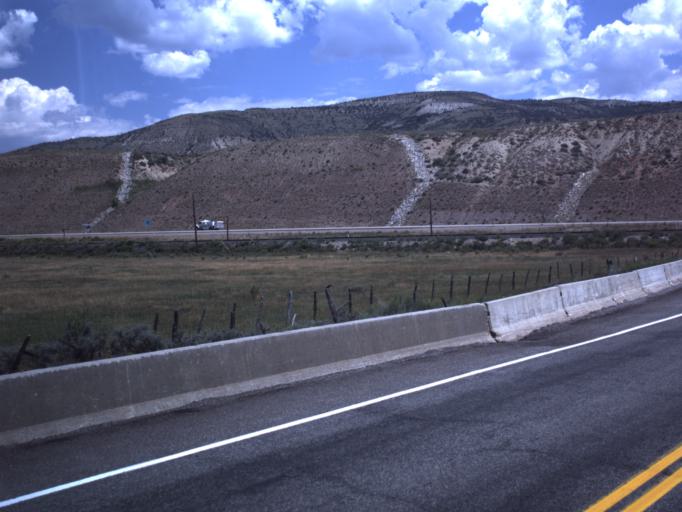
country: US
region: Utah
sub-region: Carbon County
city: Helper
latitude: 39.8613
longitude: -111.0286
